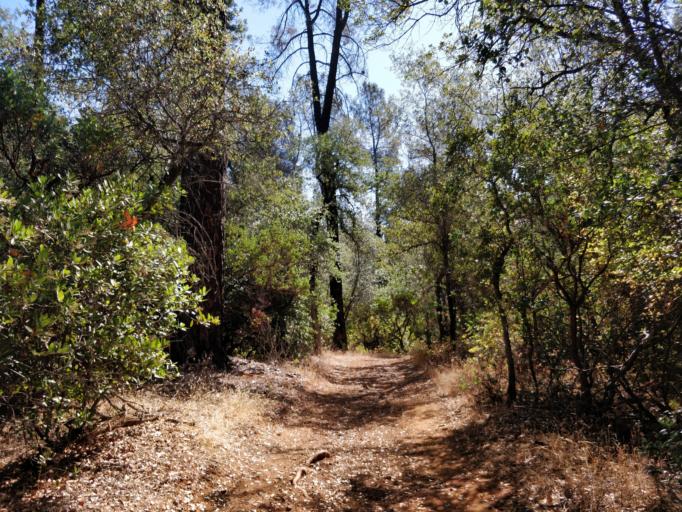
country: US
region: California
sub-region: Shasta County
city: Central Valley (historical)
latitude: 40.6671
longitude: -122.3934
